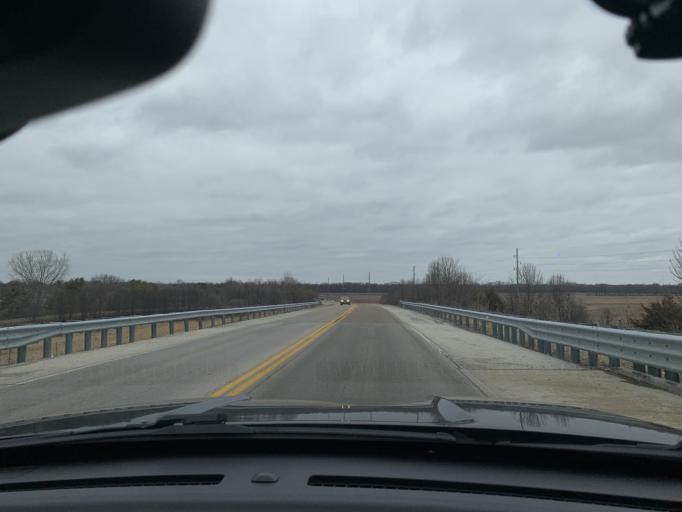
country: US
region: Illinois
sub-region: Sangamon County
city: Jerome
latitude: 39.7429
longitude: -89.6870
